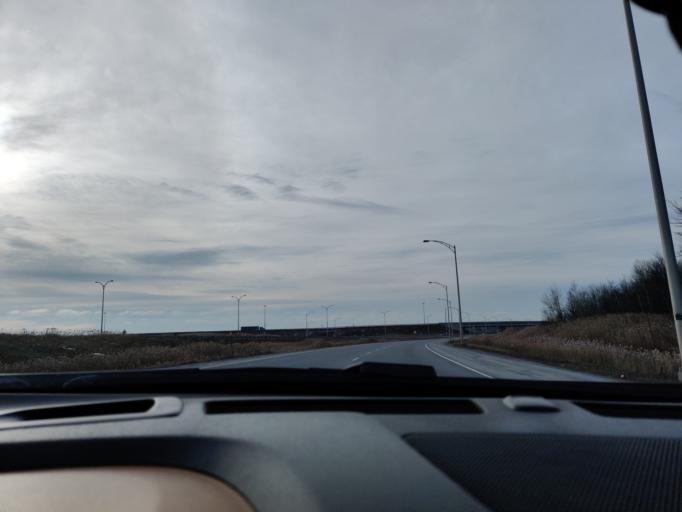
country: CA
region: Quebec
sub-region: Monteregie
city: Vaudreuil-Dorion
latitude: 45.3589
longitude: -74.0503
